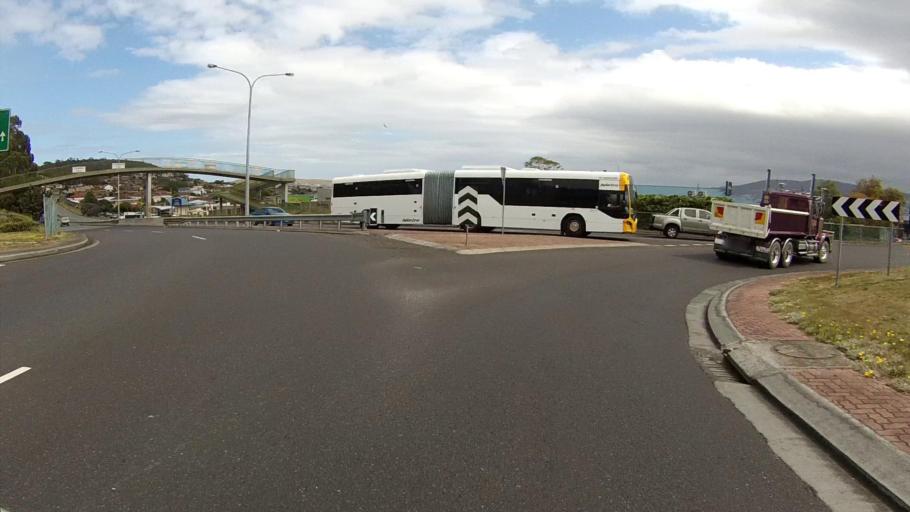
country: AU
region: Tasmania
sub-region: Clarence
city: Howrah
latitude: -42.8782
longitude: 147.4068
